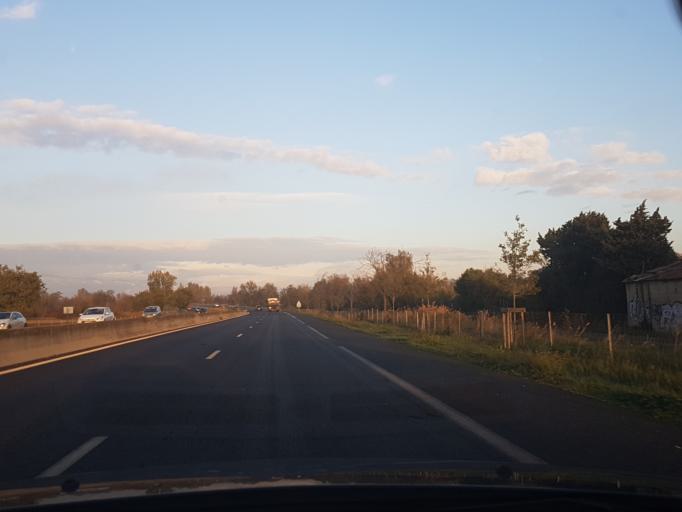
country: FR
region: Provence-Alpes-Cote d'Azur
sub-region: Departement du Vaucluse
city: Entraigues-sur-la-Sorgue
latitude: 43.9953
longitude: 4.9349
